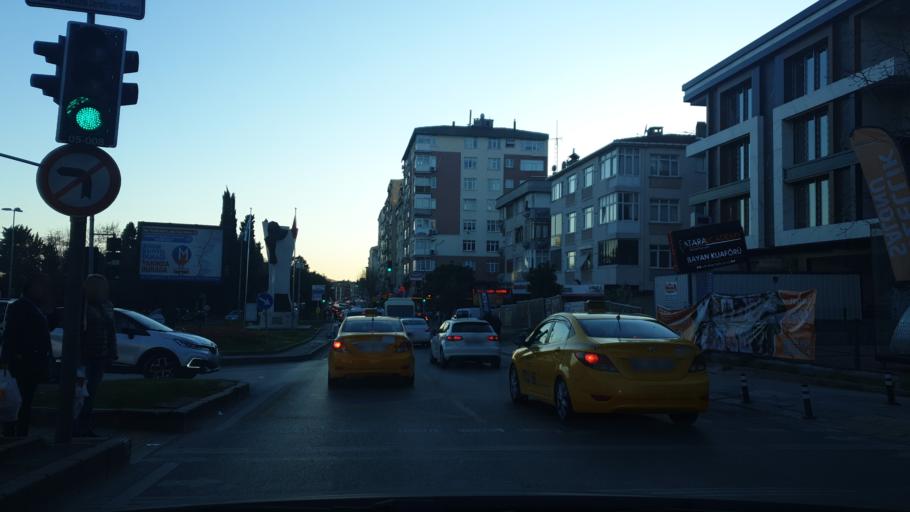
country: TR
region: Istanbul
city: Bahcelievler
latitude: 40.9993
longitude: 28.8590
